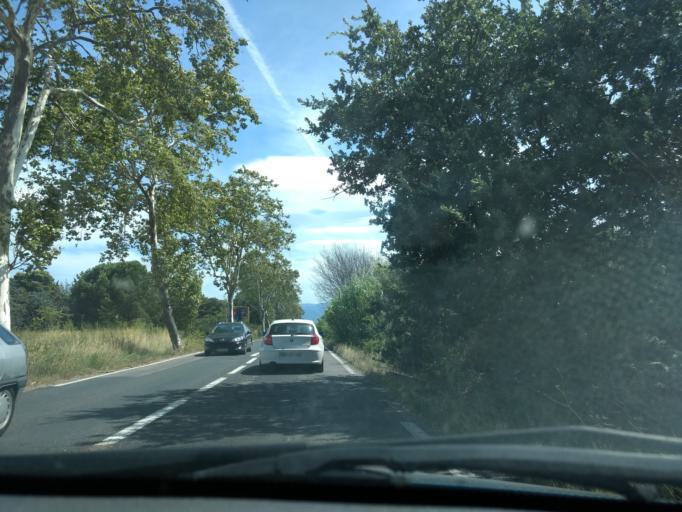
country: FR
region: Languedoc-Roussillon
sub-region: Departement des Pyrenees-Orientales
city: Cabestany
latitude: 42.6724
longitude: 2.9155
